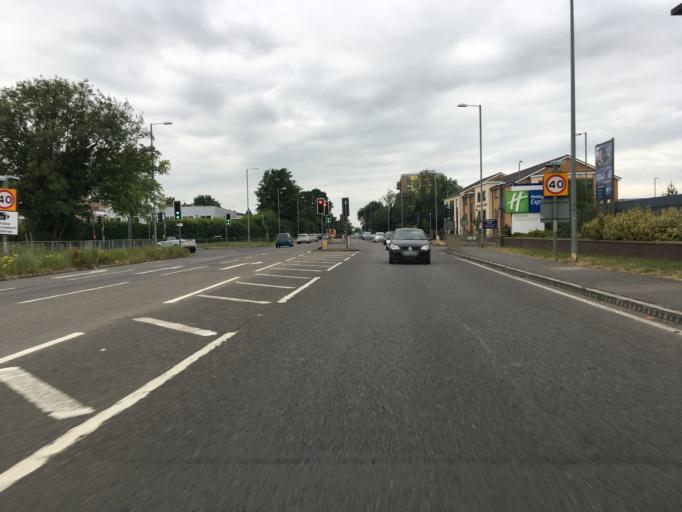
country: GB
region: England
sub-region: Central Bedfordshire
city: Kensworth
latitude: 51.8730
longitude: -0.5009
